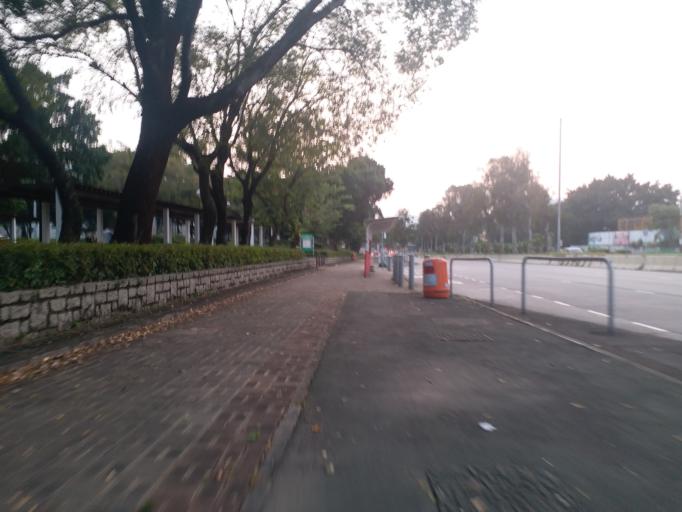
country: HK
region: Yuen Long
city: Yuen Long Kau Hui
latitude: 22.4419
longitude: 114.0108
